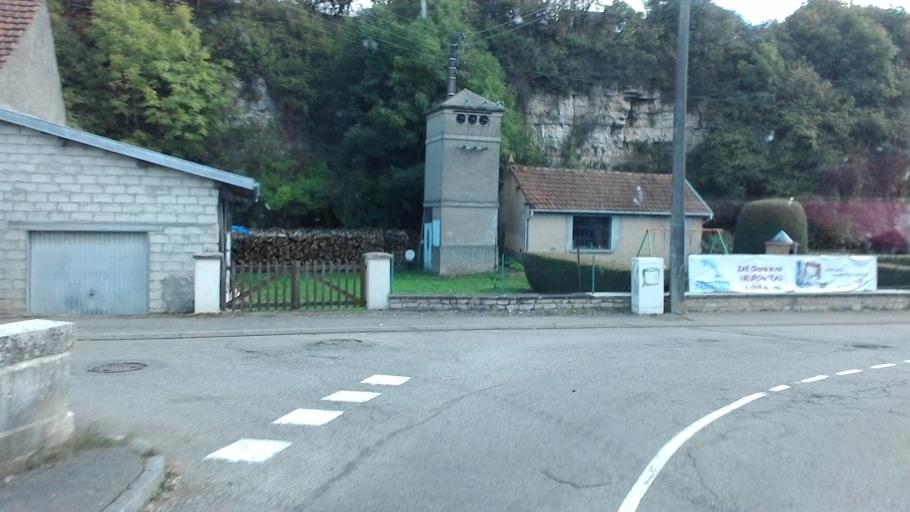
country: FR
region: Lorraine
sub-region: Departement des Vosges
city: Neufchateau
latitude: 48.3666
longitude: 5.6893
